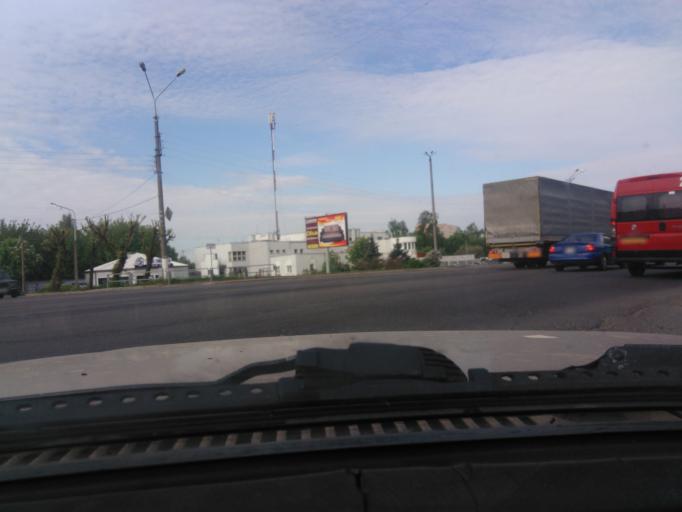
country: BY
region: Mogilev
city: Mahilyow
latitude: 53.9185
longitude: 30.3061
